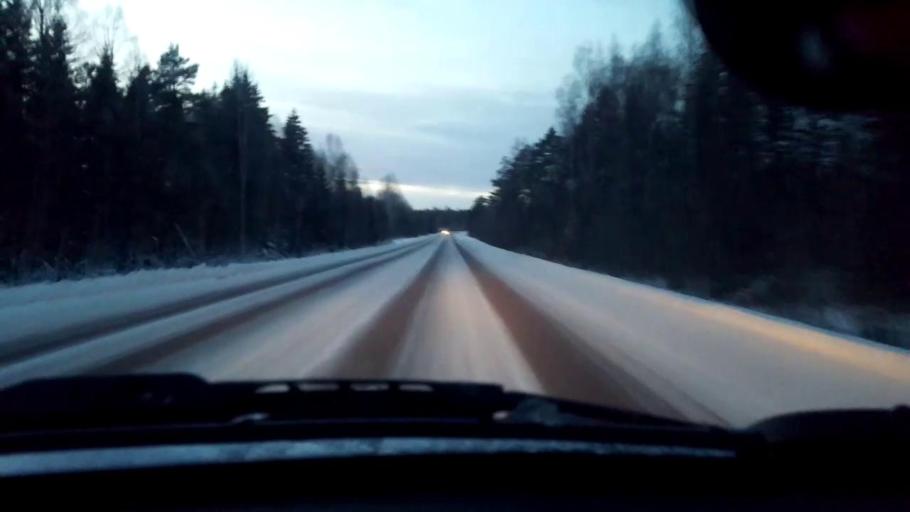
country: SE
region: Dalarna
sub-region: Mora Kommun
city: Mora
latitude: 60.9388
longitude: 14.5461
